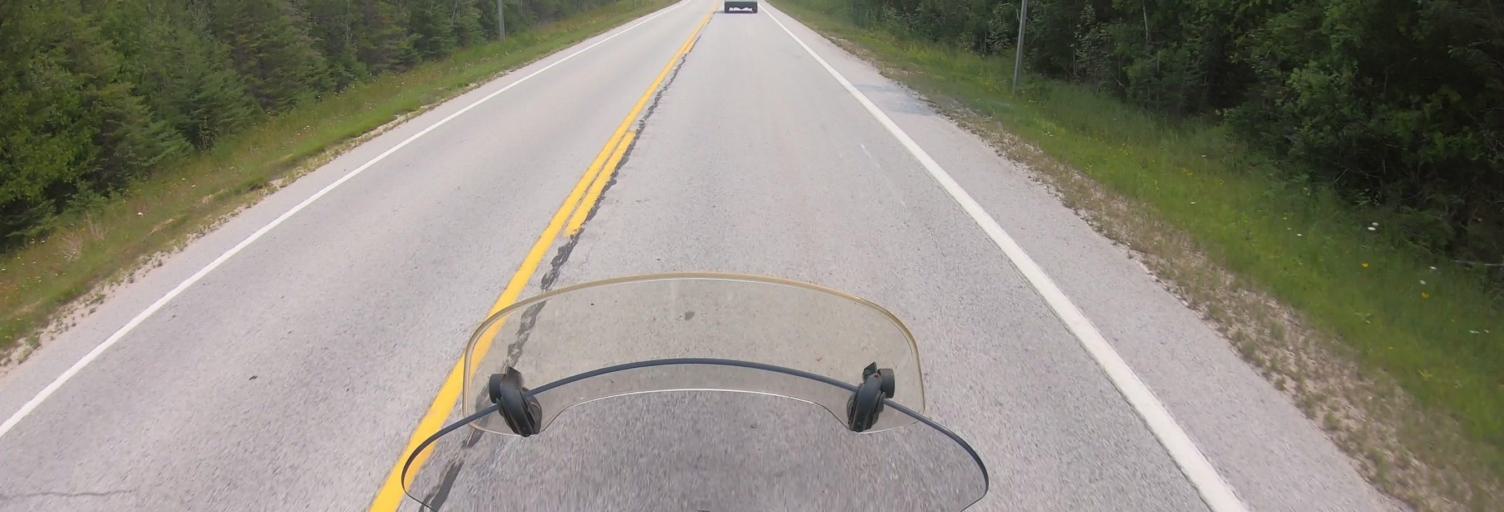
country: CA
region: Ontario
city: Thessalon
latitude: 45.9968
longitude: -83.8475
